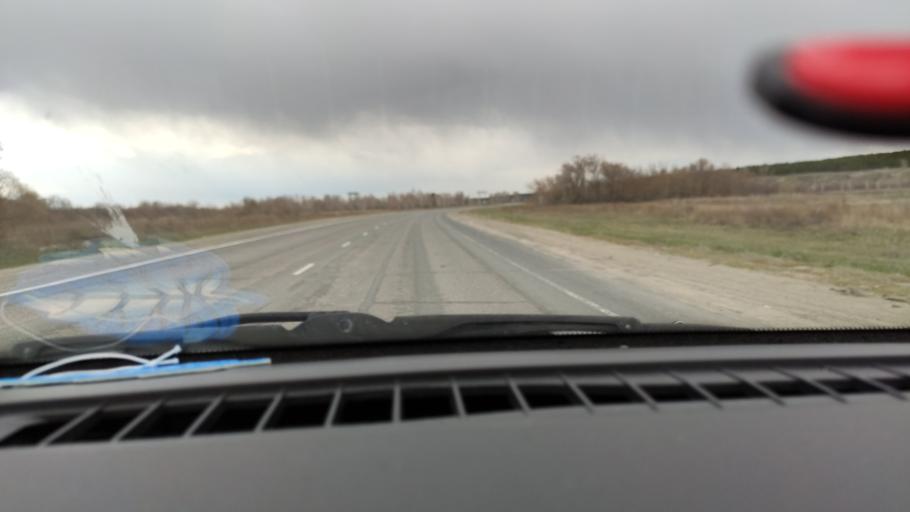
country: RU
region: Saratov
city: Sinodskoye
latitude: 52.0409
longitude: 46.7343
